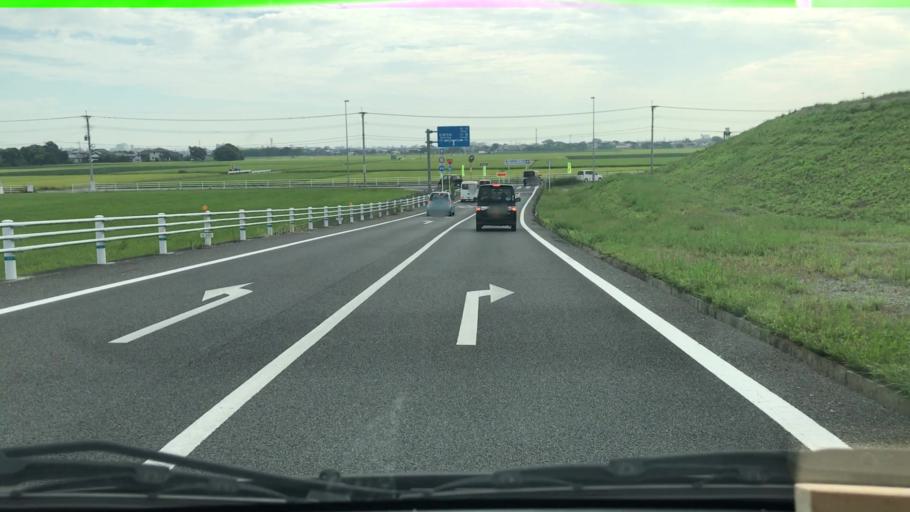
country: JP
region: Saga Prefecture
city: Saga-shi
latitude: 33.2317
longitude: 130.2565
